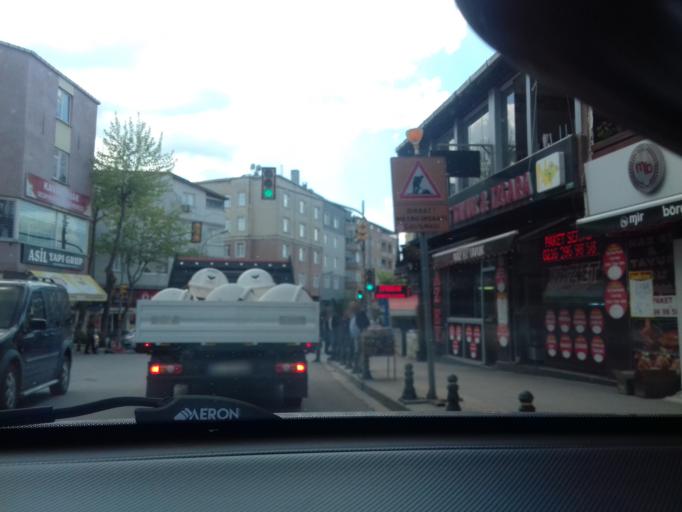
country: TR
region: Istanbul
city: Pendik
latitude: 40.8763
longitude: 29.2857
